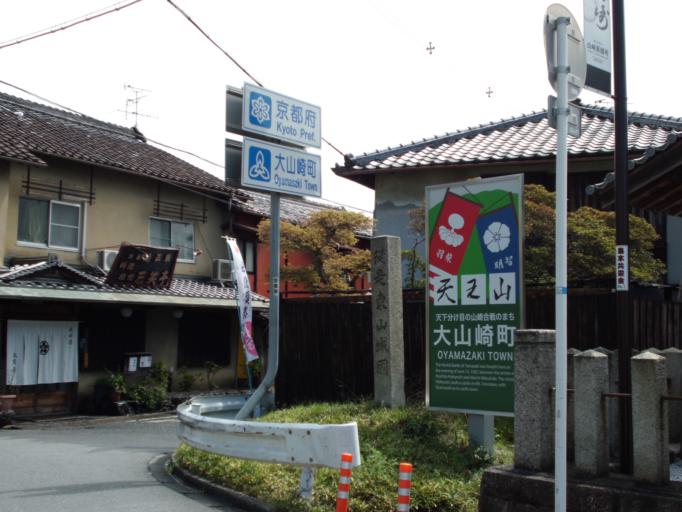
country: JP
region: Kyoto
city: Yawata
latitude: 34.8916
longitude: 135.6789
